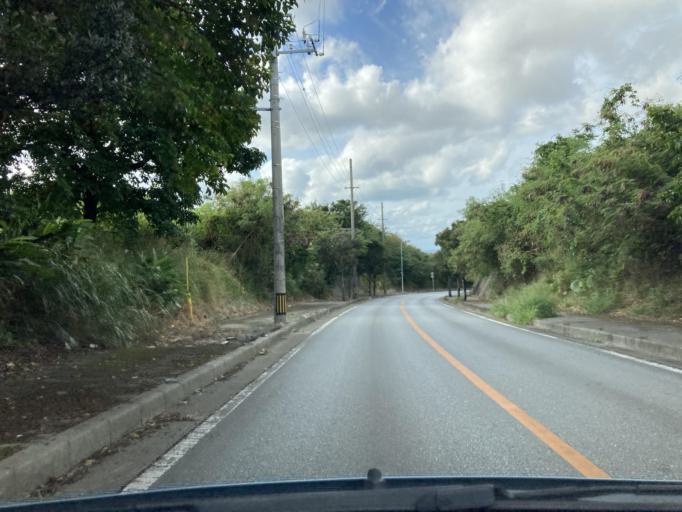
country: JP
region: Okinawa
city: Itoman
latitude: 26.1270
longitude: 127.7123
